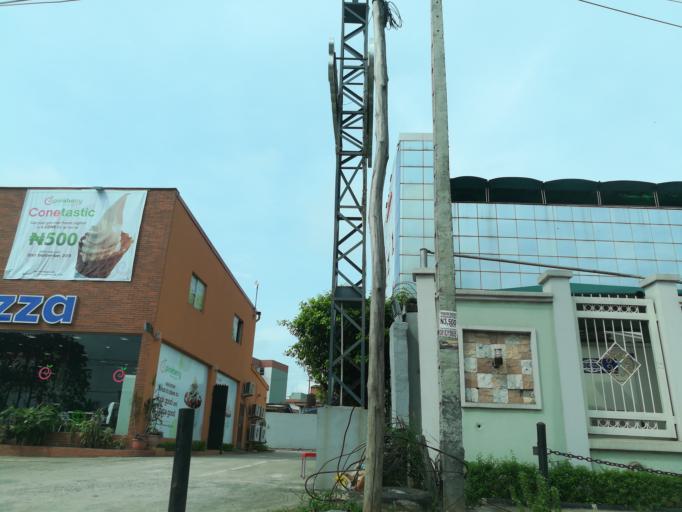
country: NG
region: Lagos
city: Ikeja
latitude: 6.6085
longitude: 3.3477
